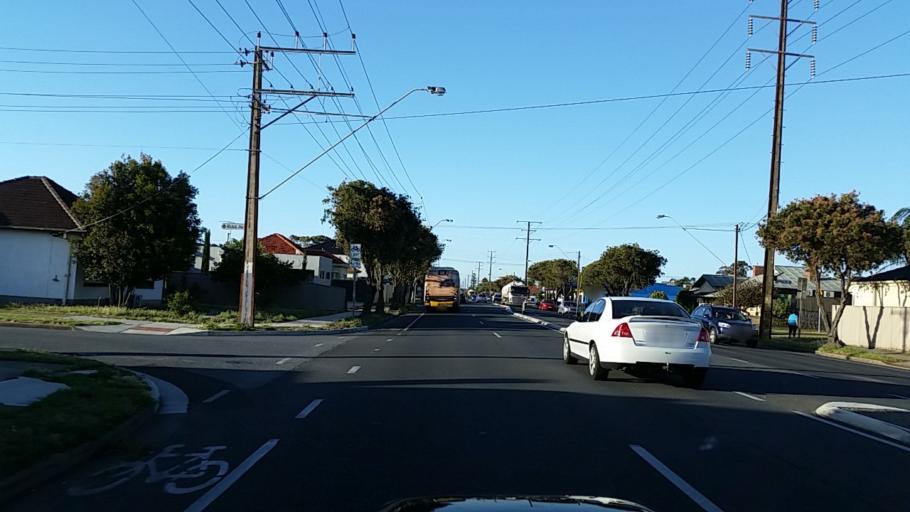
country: AU
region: South Australia
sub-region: Charles Sturt
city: Seaton
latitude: -34.8879
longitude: 138.5134
